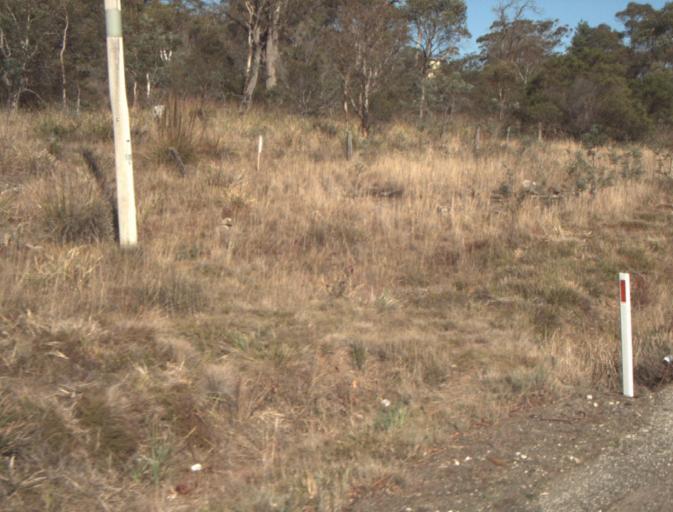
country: AU
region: Tasmania
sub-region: Launceston
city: Mayfield
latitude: -41.3441
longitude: 147.1407
